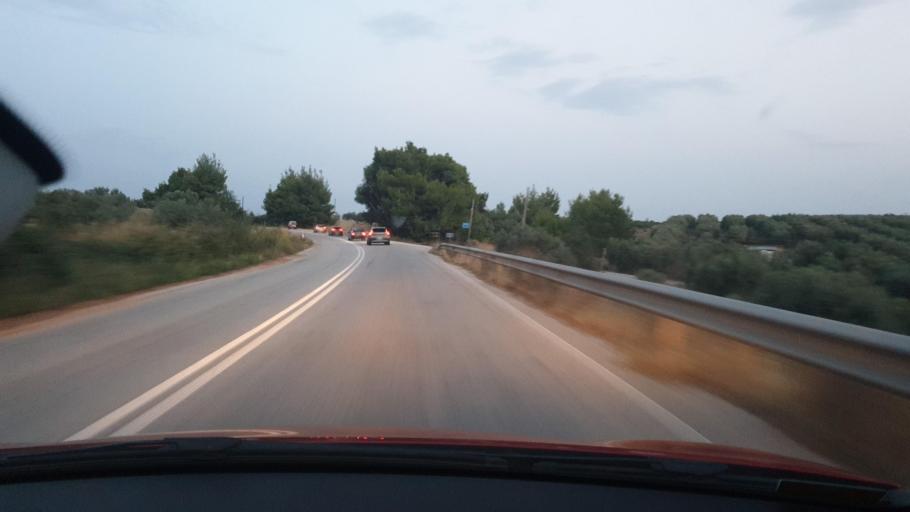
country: GR
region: Central Macedonia
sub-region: Nomos Chalkidikis
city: Ormylia
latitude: 40.2403
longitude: 23.5872
